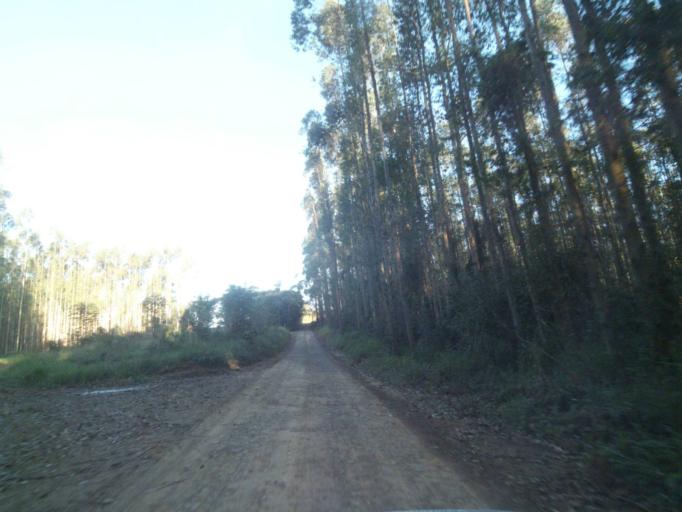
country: BR
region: Parana
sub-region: Telemaco Borba
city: Telemaco Borba
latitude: -24.4976
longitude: -50.5999
